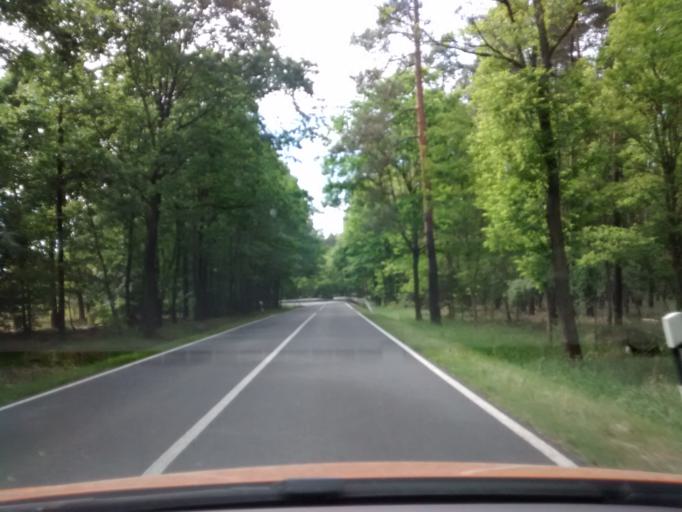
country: DE
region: Brandenburg
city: Luckenwalde
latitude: 51.9937
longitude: 13.2541
